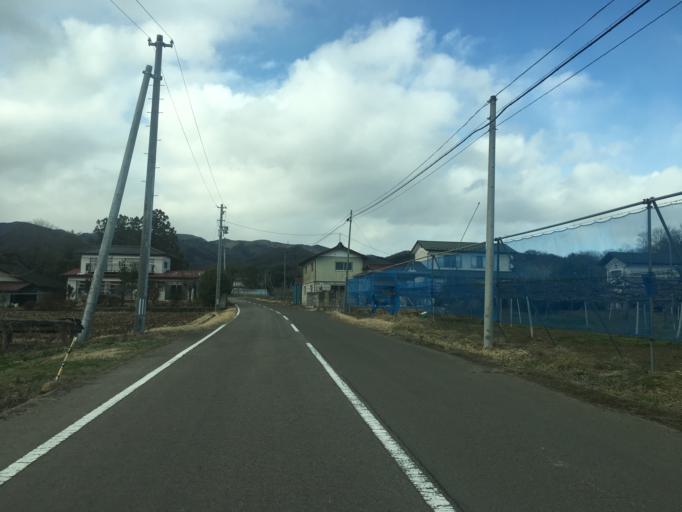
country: JP
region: Fukushima
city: Yanagawamachi-saiwaicho
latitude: 37.8792
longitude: 140.5970
